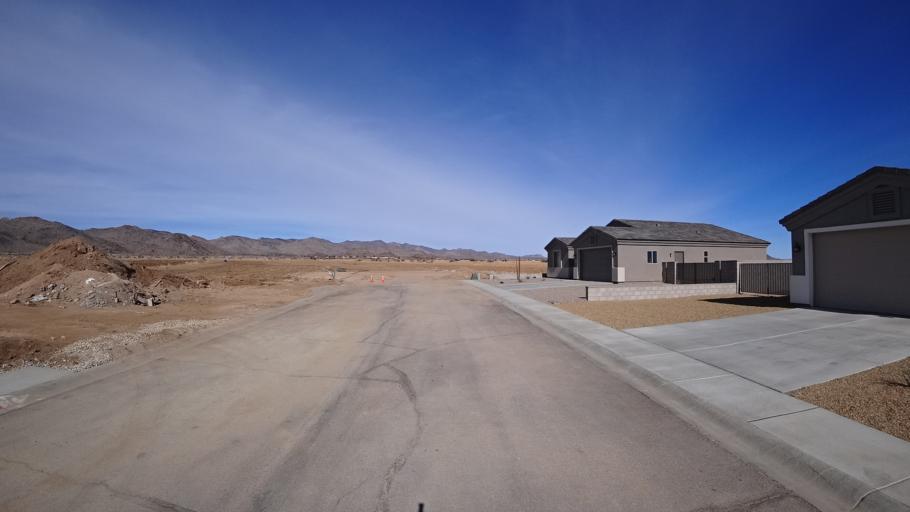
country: US
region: Arizona
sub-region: Mohave County
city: New Kingman-Butler
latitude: 35.2778
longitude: -114.0363
